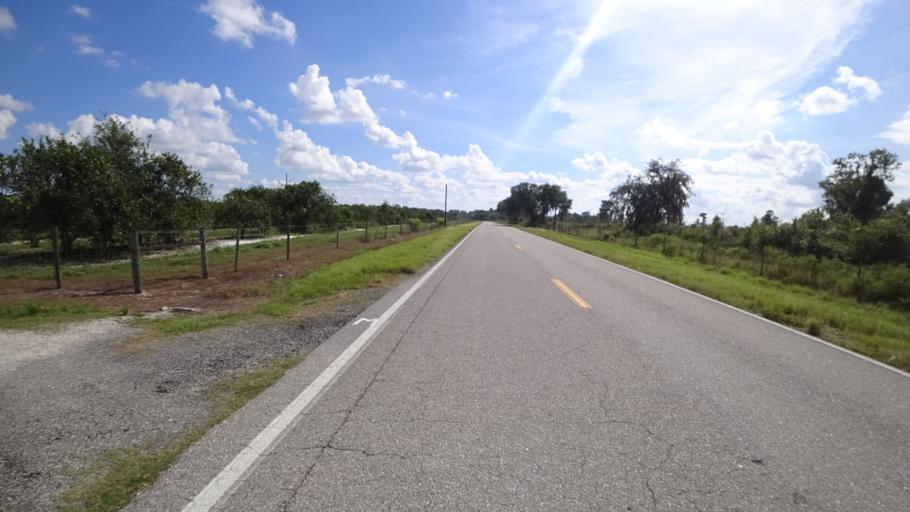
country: US
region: Florida
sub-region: Hillsborough County
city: Wimauma
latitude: 27.5466
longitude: -82.1039
